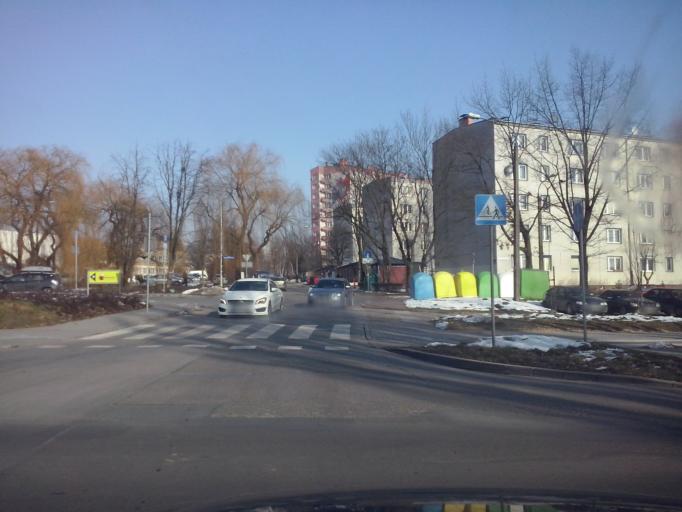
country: PL
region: Lesser Poland Voivodeship
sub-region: Krakow
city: Krakow
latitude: 50.0870
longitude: 20.0073
